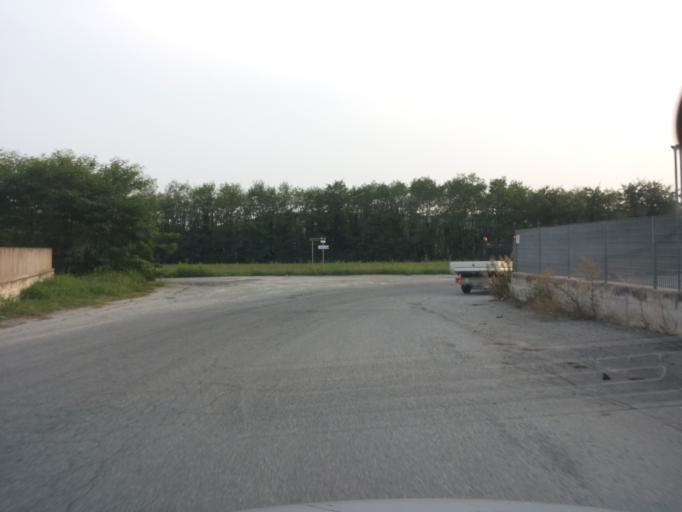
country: IT
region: Piedmont
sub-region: Provincia di Biella
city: Cavaglia
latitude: 45.3816
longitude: 8.1206
